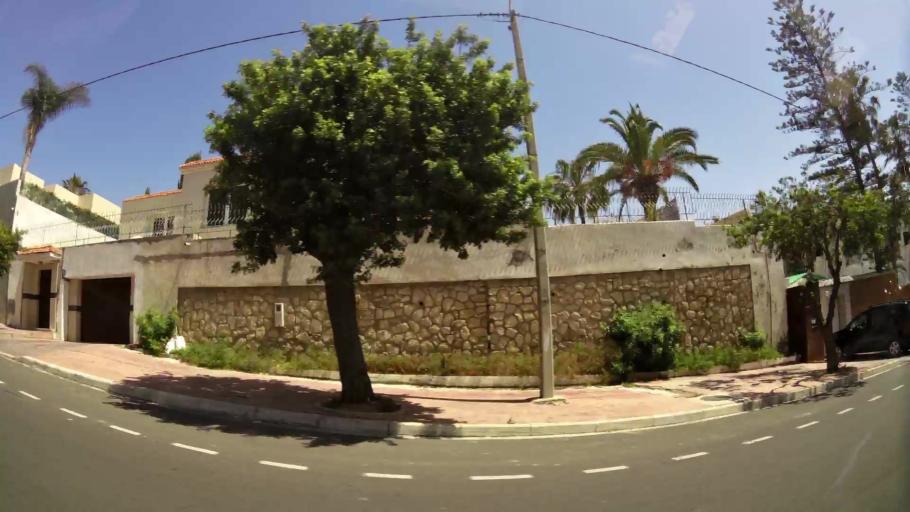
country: MA
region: Souss-Massa-Draa
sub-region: Agadir-Ida-ou-Tnan
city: Agadir
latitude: 30.4292
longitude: -9.6010
